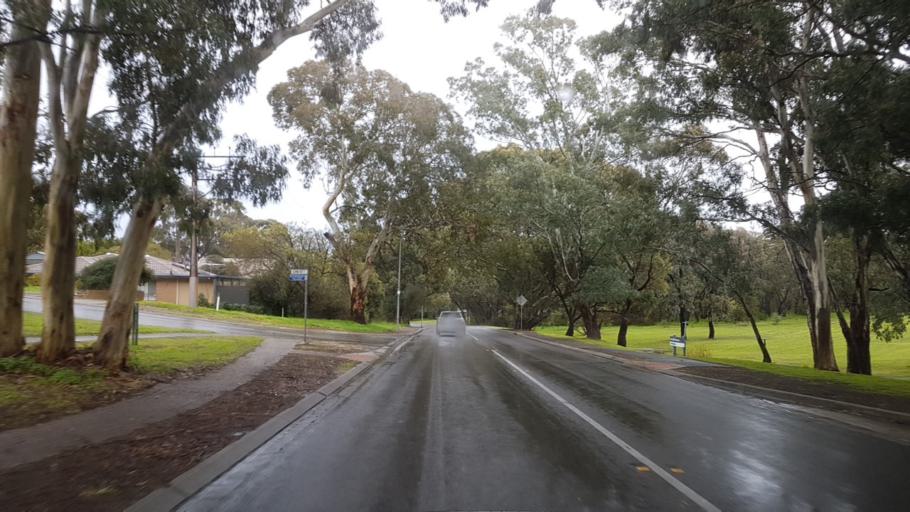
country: AU
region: South Australia
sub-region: Onkaparinga
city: Craigburn Farm
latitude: -35.0590
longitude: 138.5995
